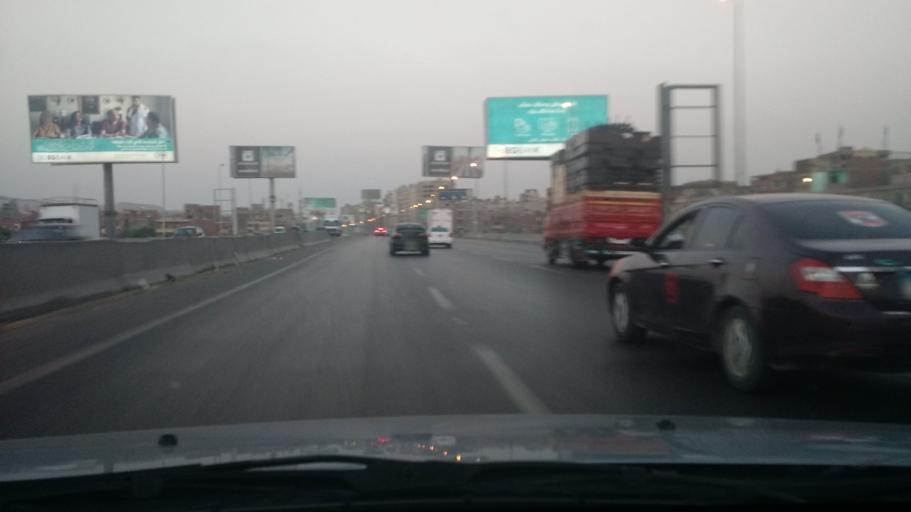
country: EG
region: Al Jizah
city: Al Jizah
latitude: 29.9903
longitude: 31.2691
